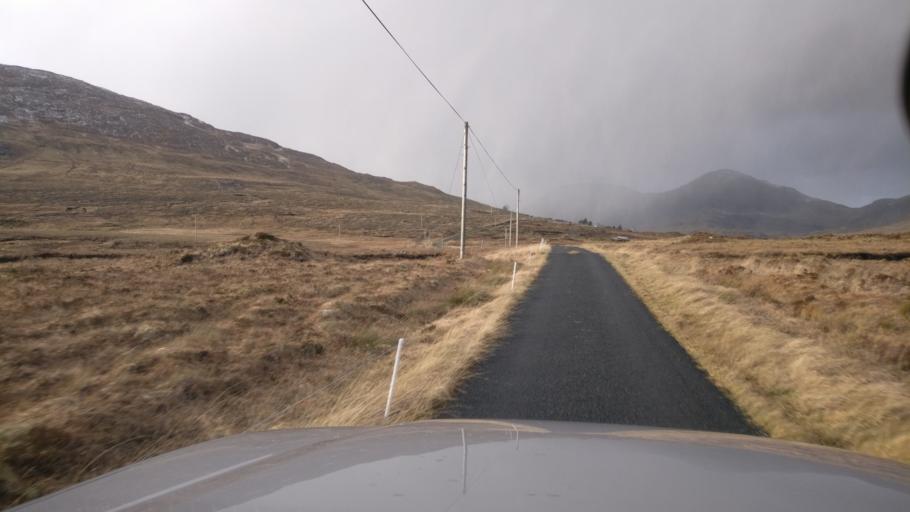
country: IE
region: Connaught
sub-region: County Galway
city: Clifden
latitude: 53.4772
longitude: -9.6931
